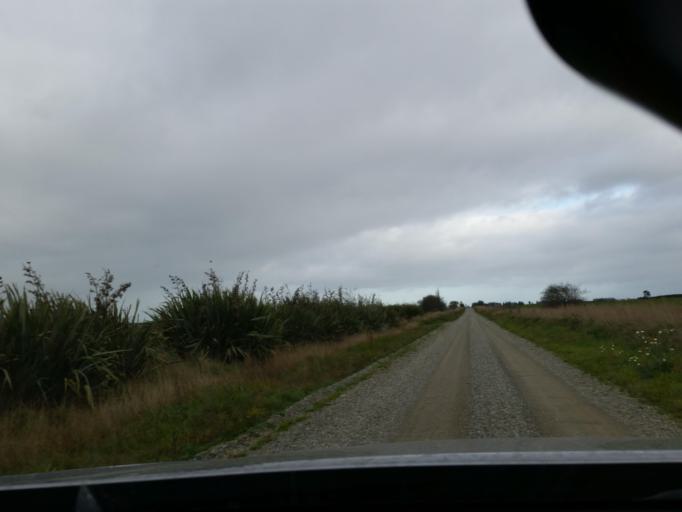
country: NZ
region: Southland
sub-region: Southland District
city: Winton
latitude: -46.2098
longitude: 168.3671
